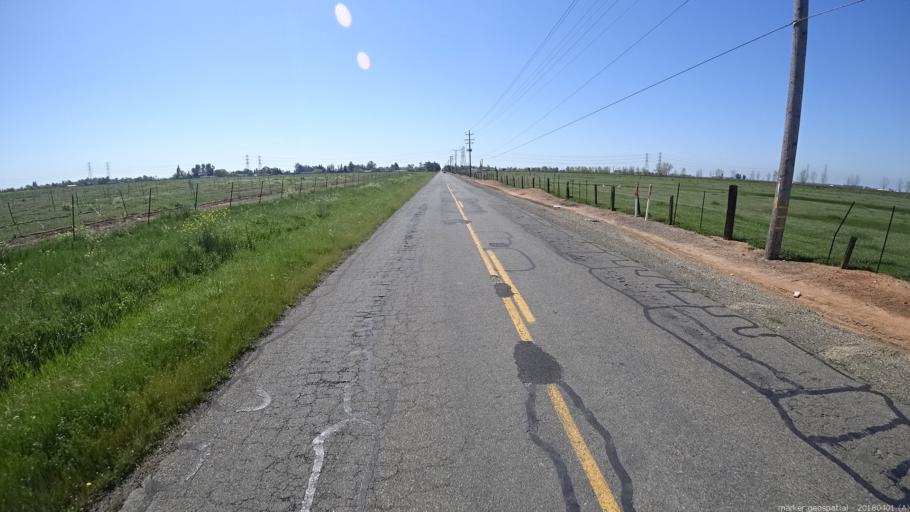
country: US
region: California
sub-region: Sacramento County
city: Herald
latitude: 38.3570
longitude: -121.2422
